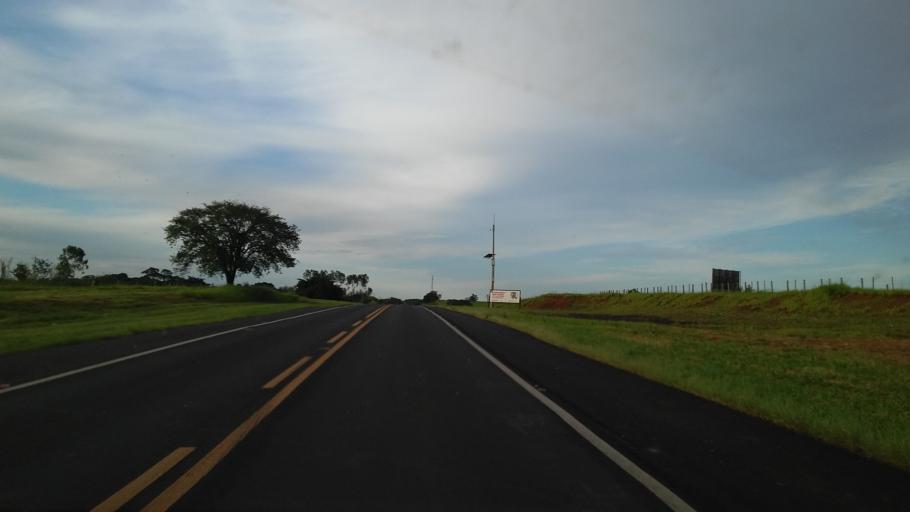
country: BR
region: Sao Paulo
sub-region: Lins
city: Lins
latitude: -21.9137
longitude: -49.9151
